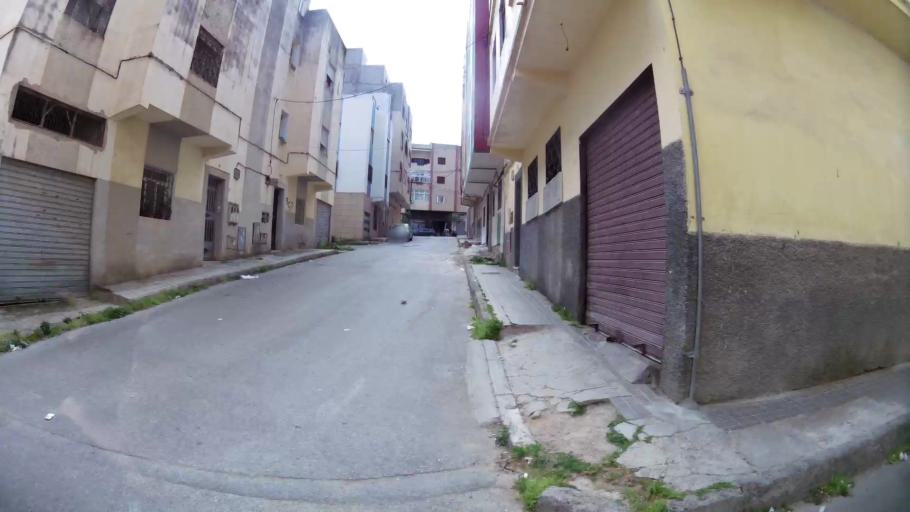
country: MA
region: Tanger-Tetouan
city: Tetouan
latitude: 35.5811
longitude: -5.3554
